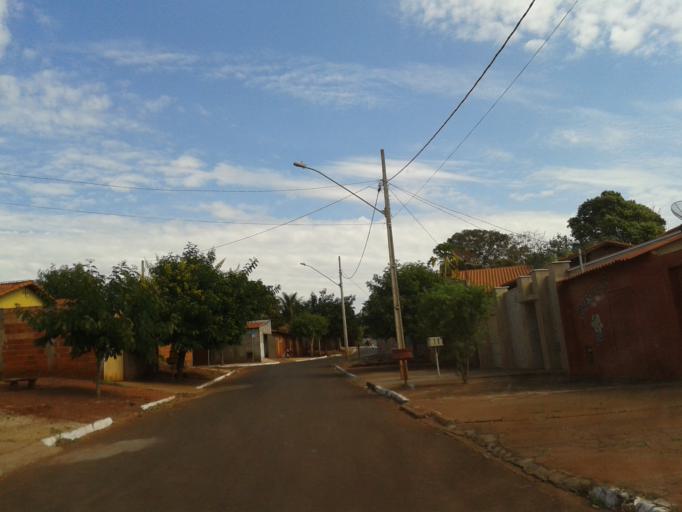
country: BR
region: Minas Gerais
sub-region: Santa Vitoria
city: Santa Vitoria
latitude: -18.8354
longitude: -50.1176
